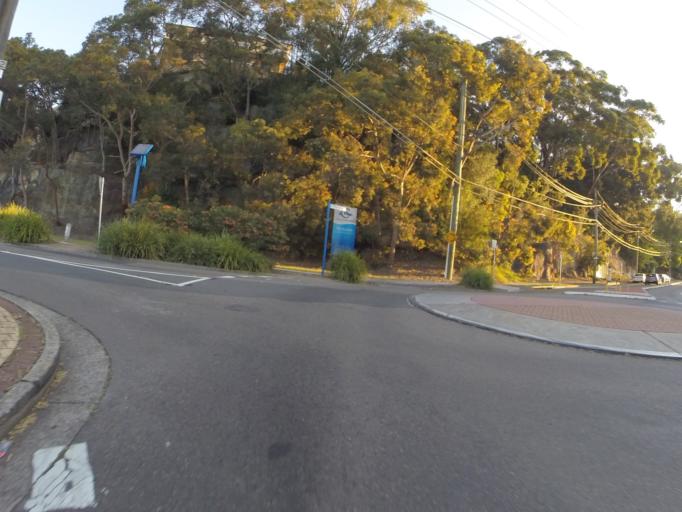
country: AU
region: New South Wales
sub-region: Rockdale
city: Bardwell Valley
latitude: -33.9234
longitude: 151.1425
